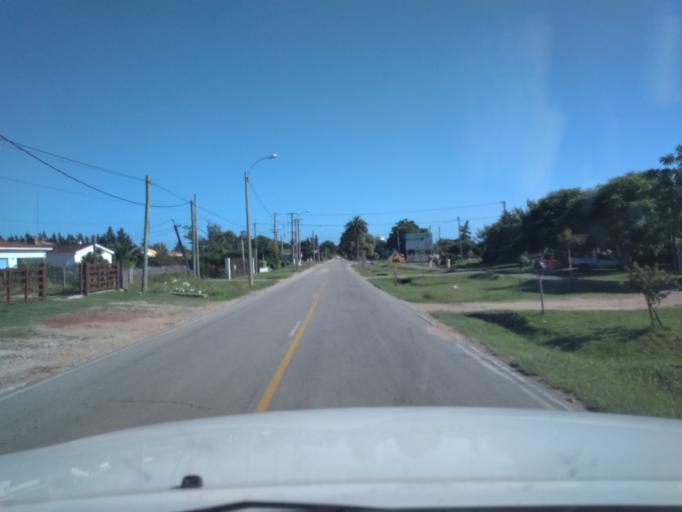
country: UY
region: Canelones
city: San Ramon
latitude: -34.3009
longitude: -55.9580
